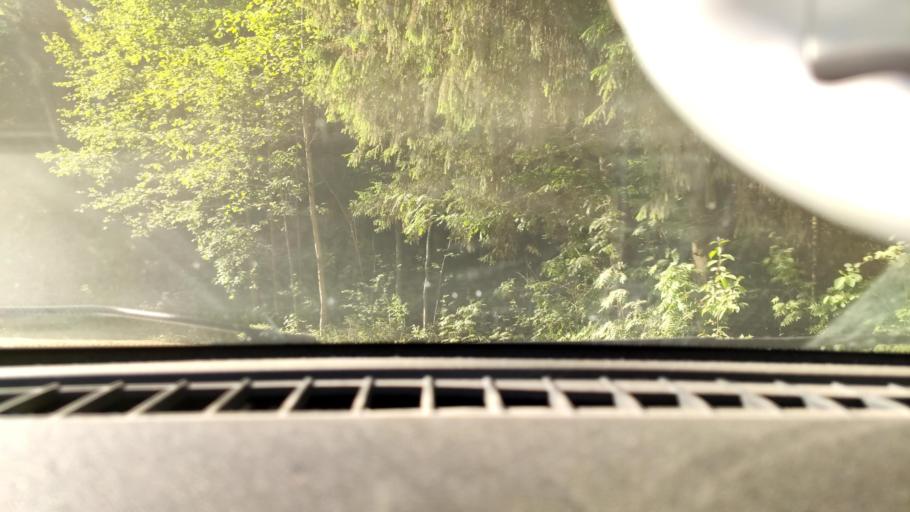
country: RU
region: Perm
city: Novyye Lyady
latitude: 58.1769
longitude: 56.5681
